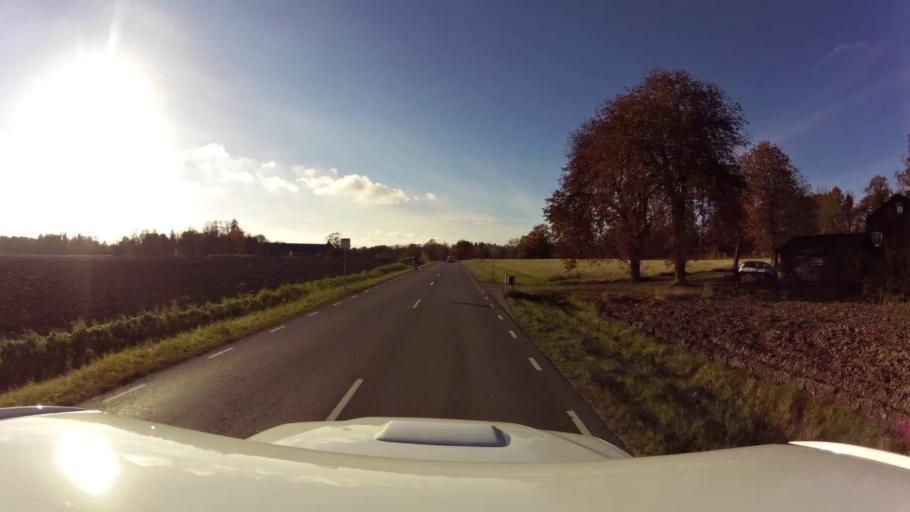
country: SE
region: OEstergoetland
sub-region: Linkopings Kommun
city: Malmslatt
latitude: 58.3471
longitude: 15.5300
